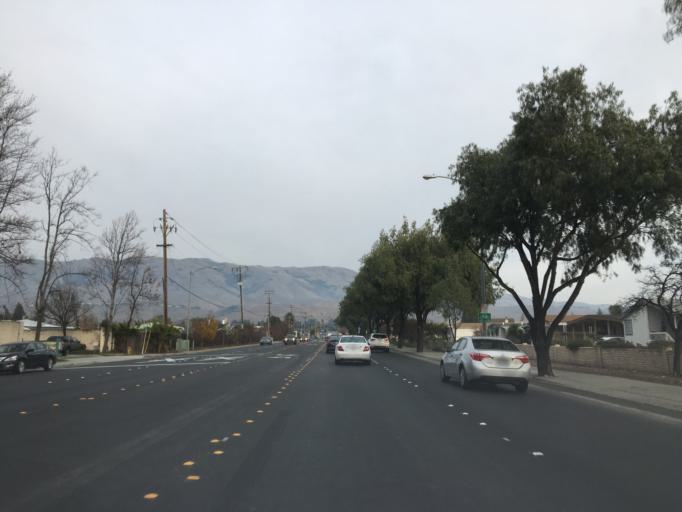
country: US
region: California
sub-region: Santa Clara County
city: Milpitas
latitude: 37.4563
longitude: -121.9152
